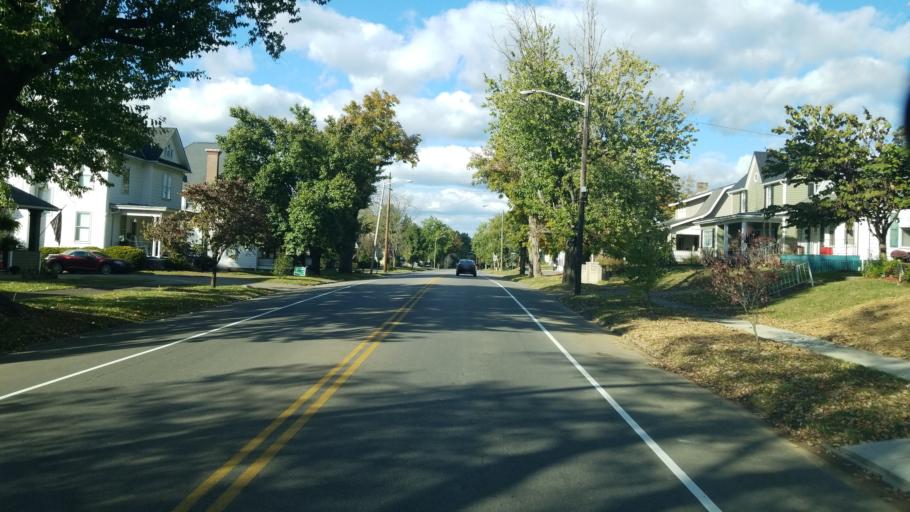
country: US
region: Ohio
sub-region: Jackson County
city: Wellston
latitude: 39.1240
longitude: -82.5328
